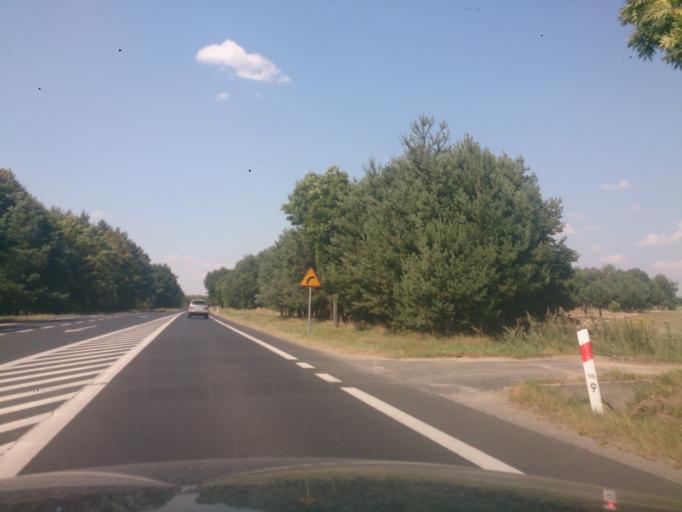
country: PL
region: Subcarpathian Voivodeship
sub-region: Powiat rzeszowski
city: Glogow Malopolski
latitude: 50.1913
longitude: 21.8922
